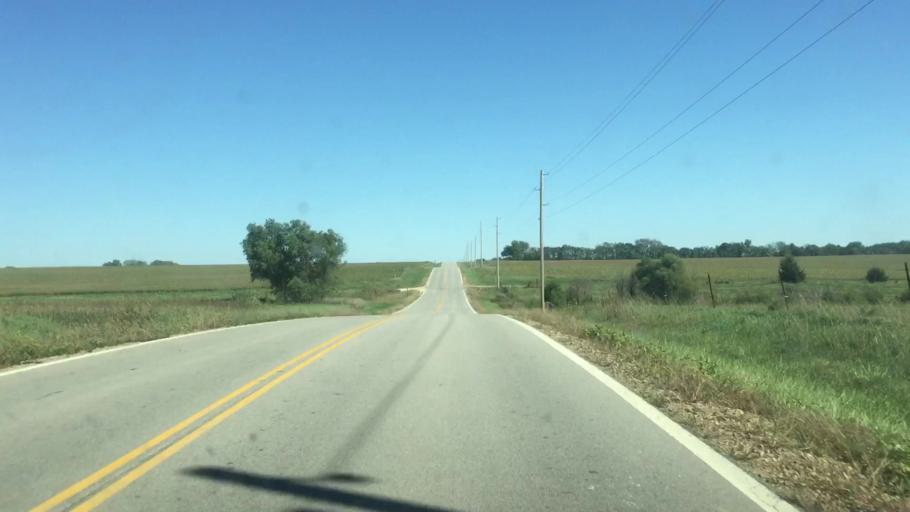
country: US
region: Kansas
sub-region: Jackson County
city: Holton
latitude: 39.5949
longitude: -95.6973
